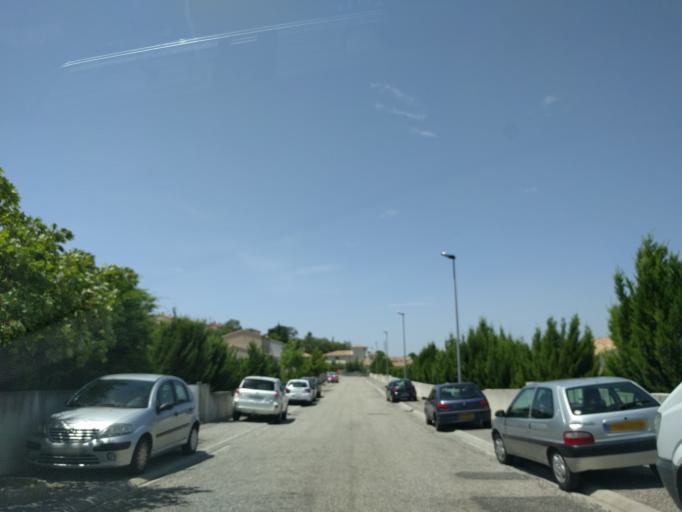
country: FR
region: Languedoc-Roussillon
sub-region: Departement de l'Aude
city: Palaja
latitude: 43.2034
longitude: 2.3985
